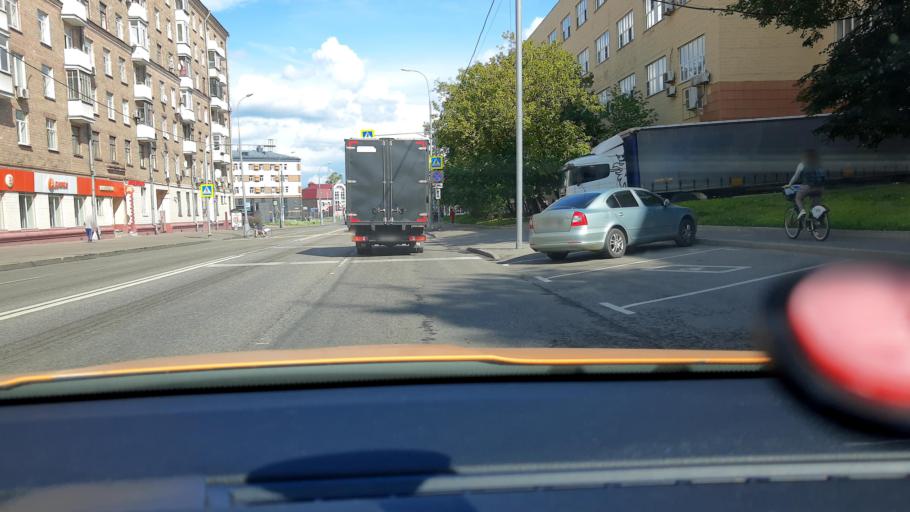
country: RU
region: Moscow
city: Mar'ina Roshcha
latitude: 55.8132
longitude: 37.5984
